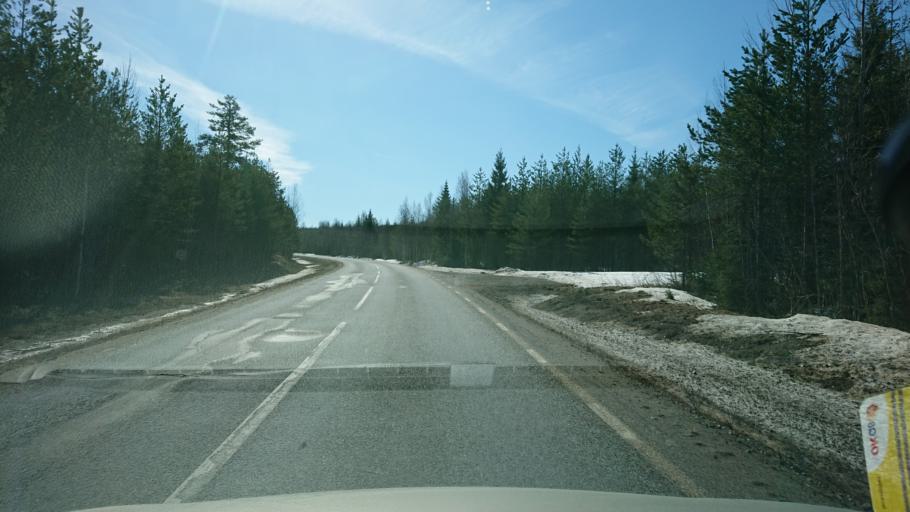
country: SE
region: Vaesterbotten
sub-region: Dorotea Kommun
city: Dorotea
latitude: 63.9990
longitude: 16.3051
